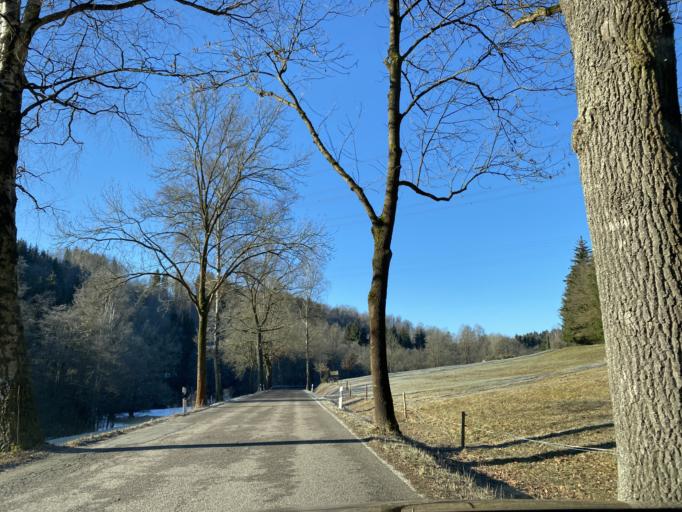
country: DE
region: Saxony
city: Wiesa
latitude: 50.6205
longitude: 13.0297
